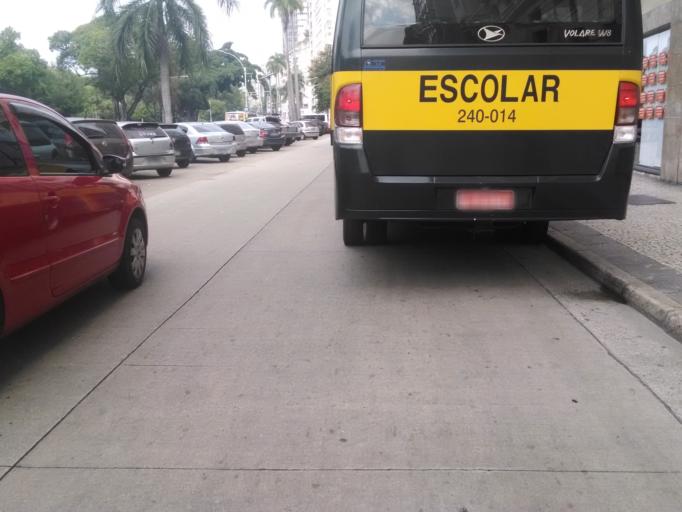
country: BR
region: Rio de Janeiro
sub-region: Rio De Janeiro
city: Rio de Janeiro
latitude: -22.9286
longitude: -43.1741
